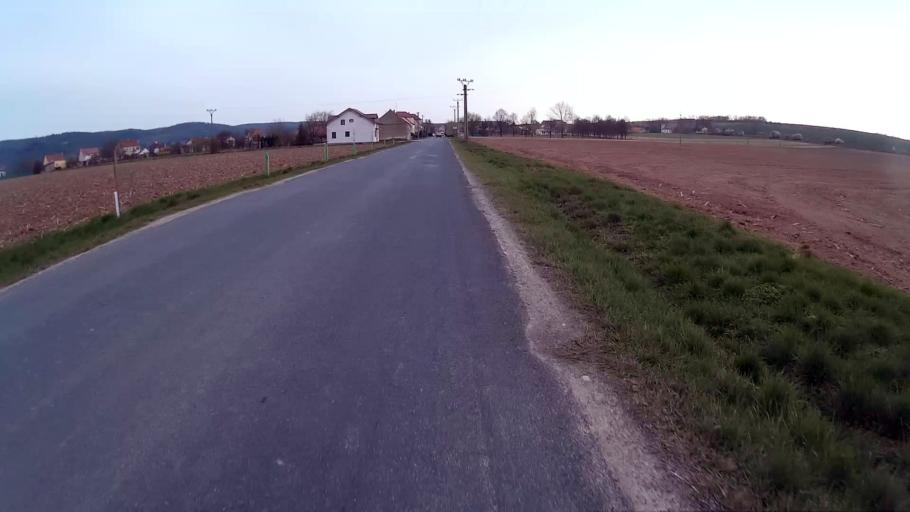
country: CZ
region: South Moravian
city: Ivancice
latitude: 49.0773
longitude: 16.3491
